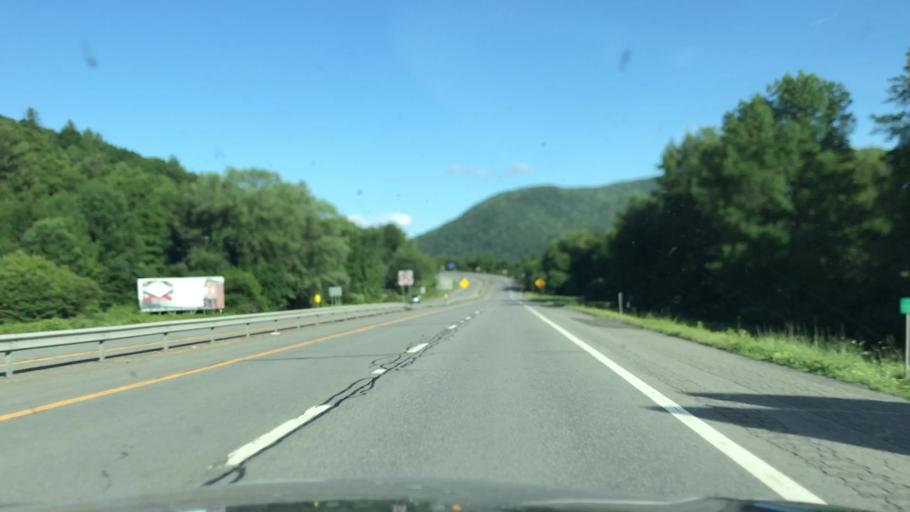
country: US
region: New York
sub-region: Delaware County
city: Hancock
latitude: 41.9968
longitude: -75.1467
